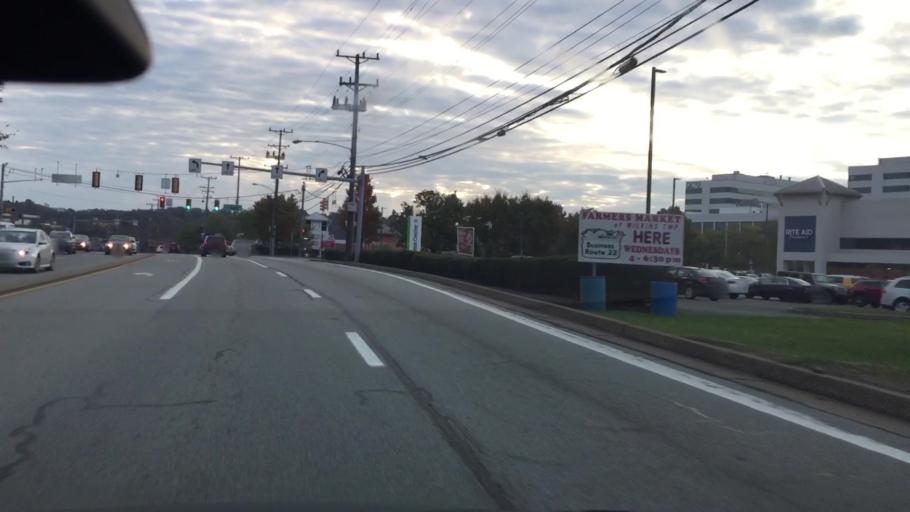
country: US
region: Pennsylvania
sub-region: Allegheny County
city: Monroeville
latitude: 40.4303
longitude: -79.8132
